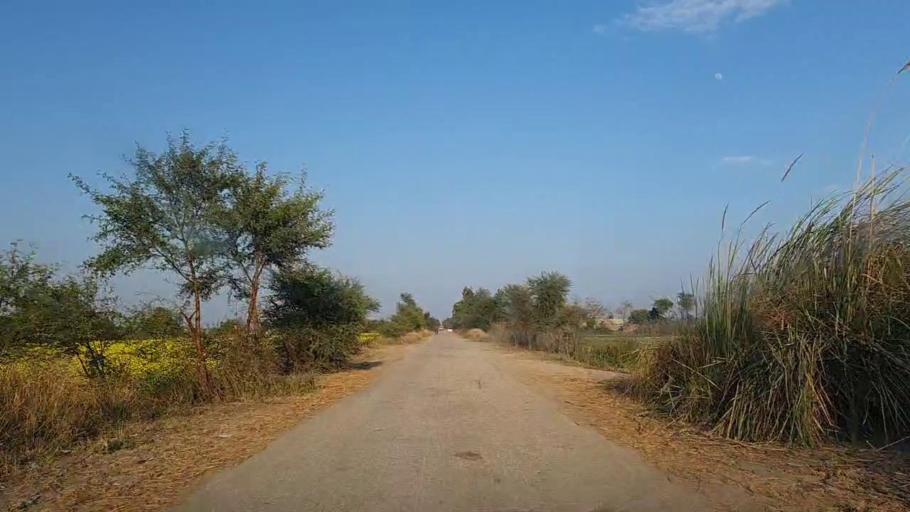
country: PK
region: Sindh
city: Sanghar
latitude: 26.2662
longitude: 68.9647
